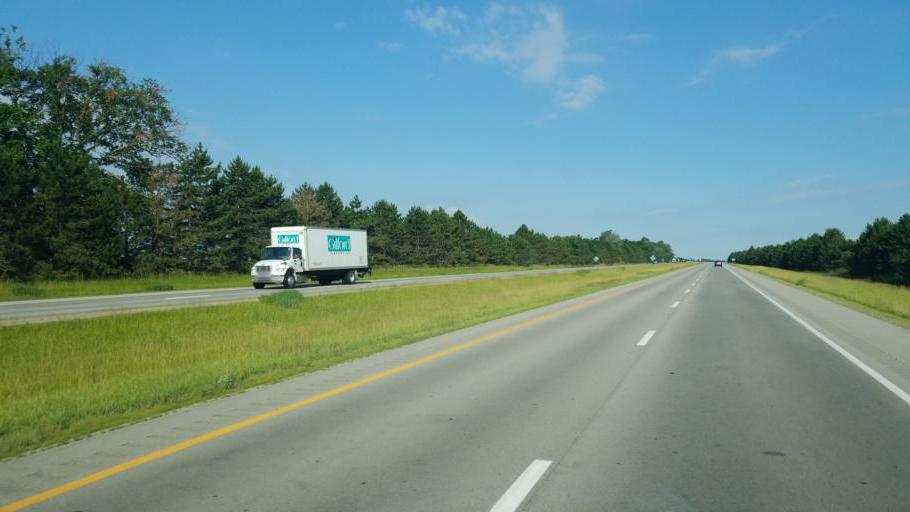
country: US
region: Ohio
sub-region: Wyandot County
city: Carey
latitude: 40.9584
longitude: -83.4519
